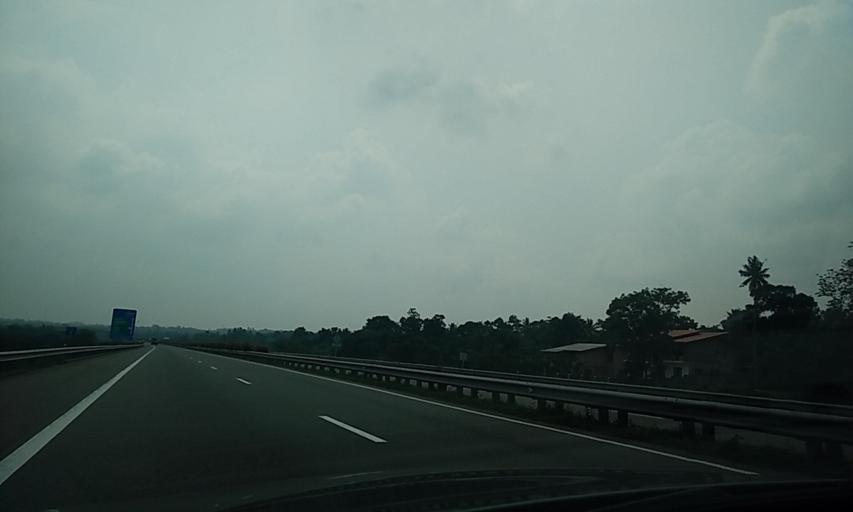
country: LK
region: Western
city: Homagama
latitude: 6.8921
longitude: 79.9779
